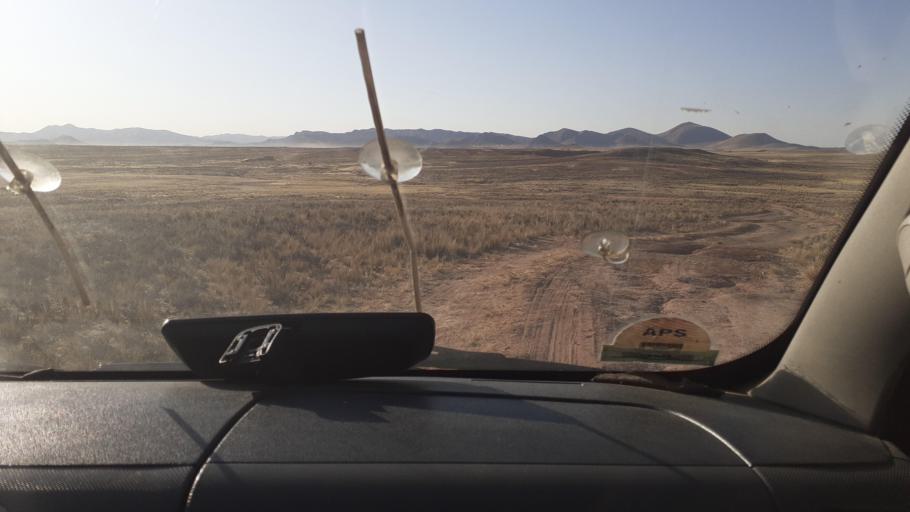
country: BO
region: La Paz
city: Tiahuanaco
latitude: -16.9958
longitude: -68.7268
